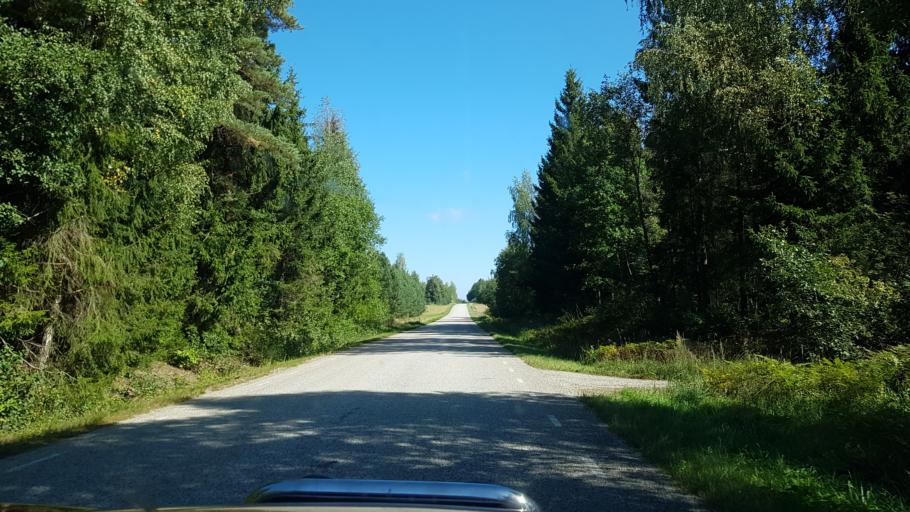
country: EE
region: Polvamaa
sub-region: Raepina vald
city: Rapina
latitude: 58.2277
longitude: 27.3003
